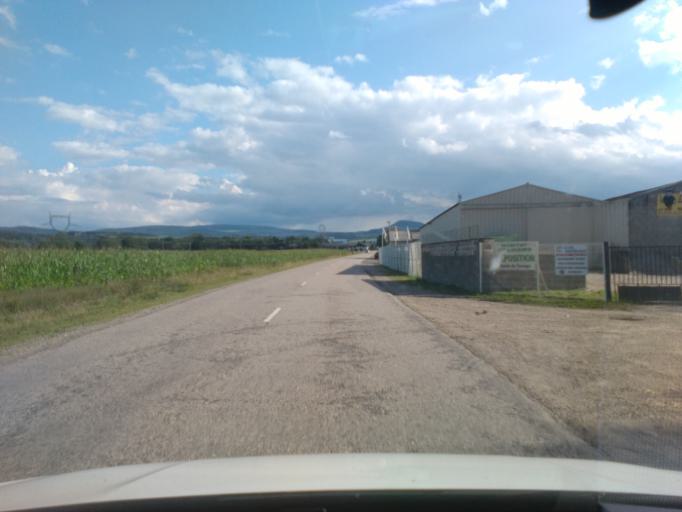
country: FR
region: Lorraine
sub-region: Departement des Vosges
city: Corcieux
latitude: 48.1931
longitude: 6.8813
